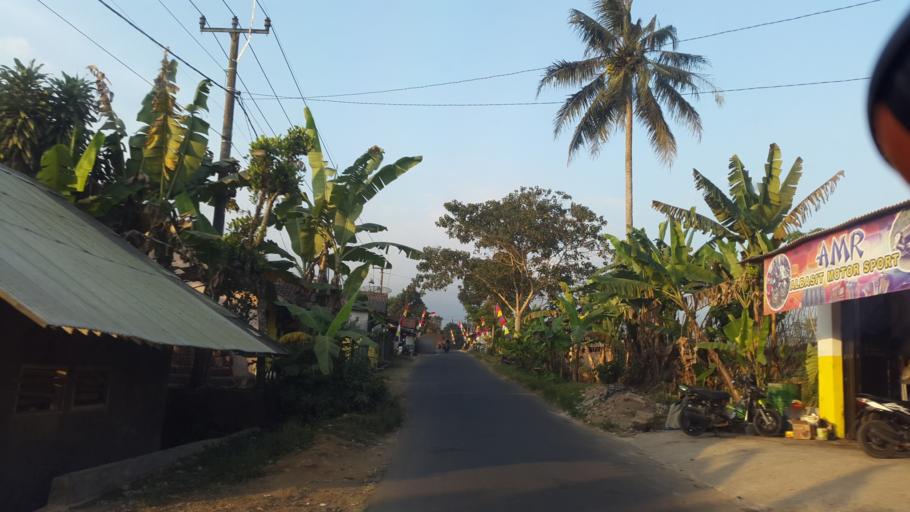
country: ID
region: West Java
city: Sukabumi
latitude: -6.8724
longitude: 106.8457
